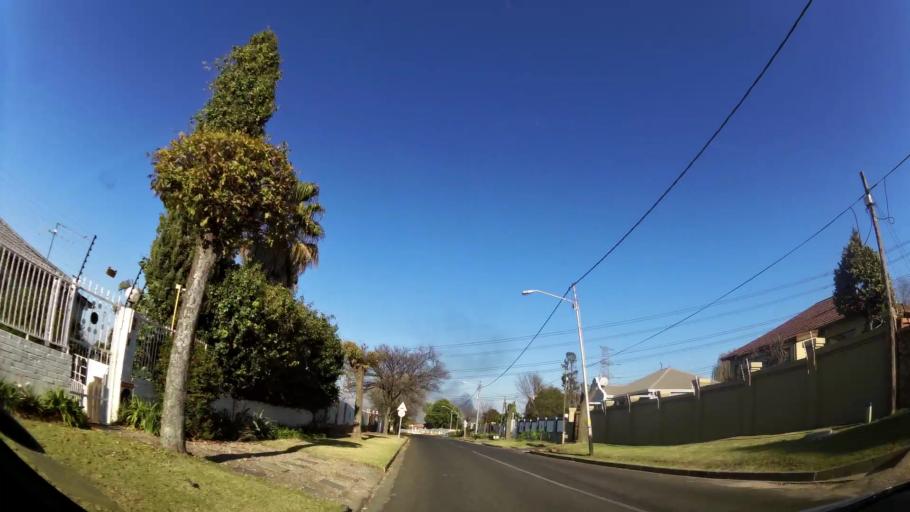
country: ZA
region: Gauteng
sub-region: Ekurhuleni Metropolitan Municipality
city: Germiston
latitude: -26.1895
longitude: 28.1470
